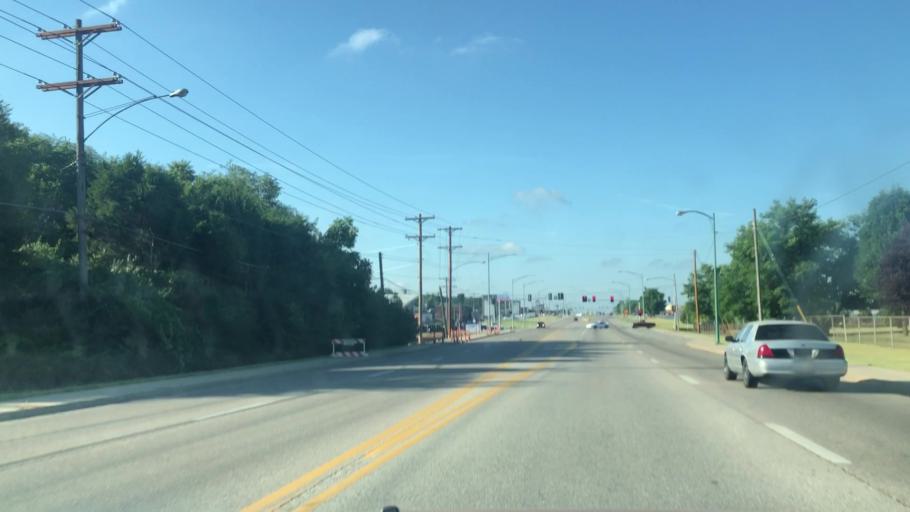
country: US
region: Missouri
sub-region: Greene County
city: Springfield
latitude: 37.1685
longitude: -93.2626
